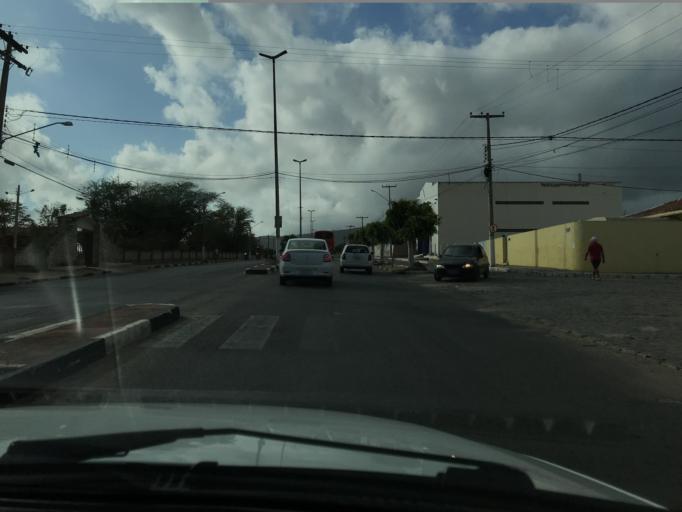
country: BR
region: Pernambuco
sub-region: Bezerros
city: Bezerros
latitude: -8.2319
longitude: -35.7452
